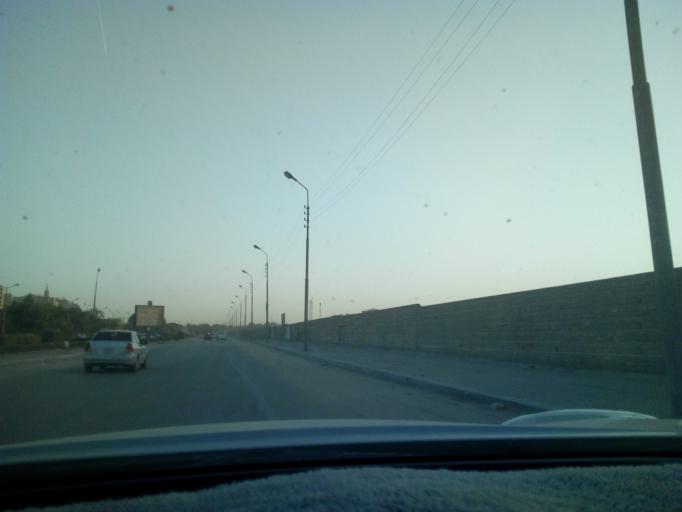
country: EG
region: Muhafazat al Qalyubiyah
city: Al Khankah
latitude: 30.1248
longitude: 31.3630
